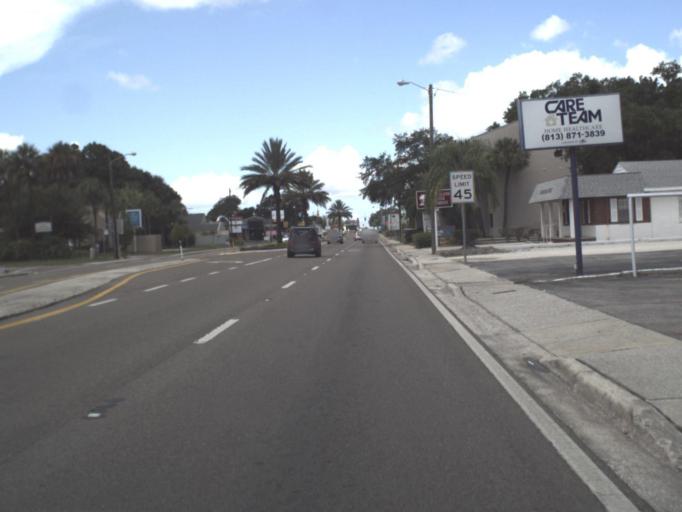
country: US
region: Florida
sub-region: Hillsborough County
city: Tampa
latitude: 27.9449
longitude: -82.4977
